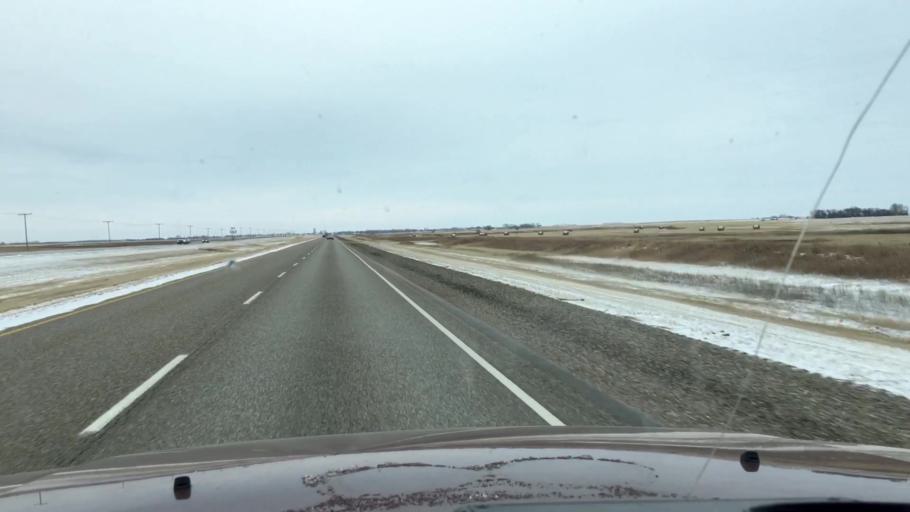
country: CA
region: Saskatchewan
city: Watrous
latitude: 51.0832
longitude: -105.8512
